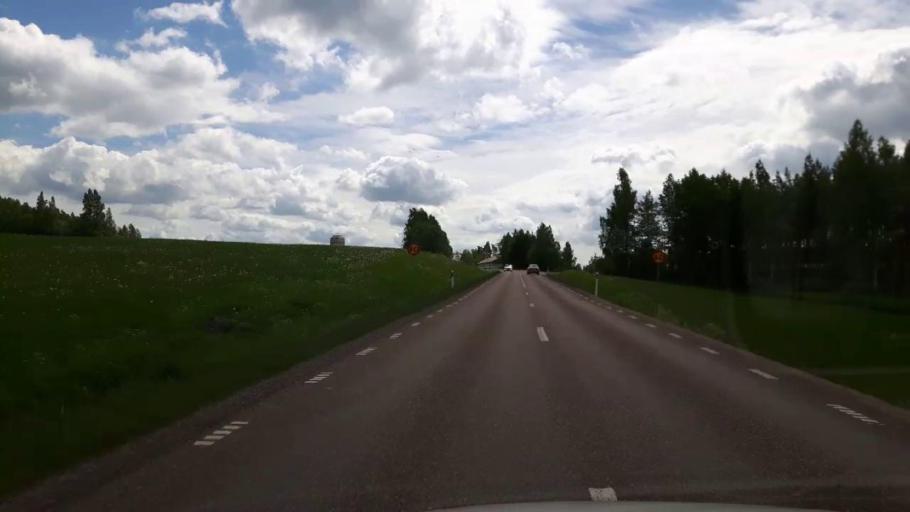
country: SE
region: Dalarna
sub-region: Saters Kommun
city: Saeter
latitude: 60.4307
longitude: 15.8319
